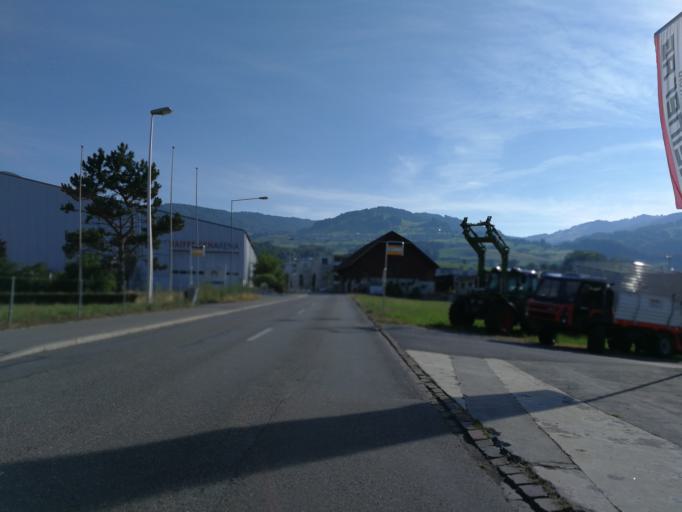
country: CH
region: Saint Gallen
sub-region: Wahlkreis See-Gaster
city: Kaltbrunn
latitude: 47.2087
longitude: 9.0222
